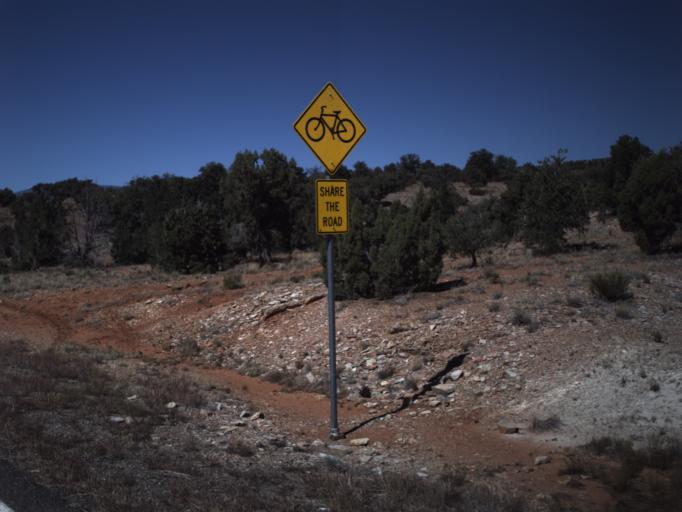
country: US
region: Utah
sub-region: Wayne County
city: Loa
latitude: 37.7281
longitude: -111.5325
